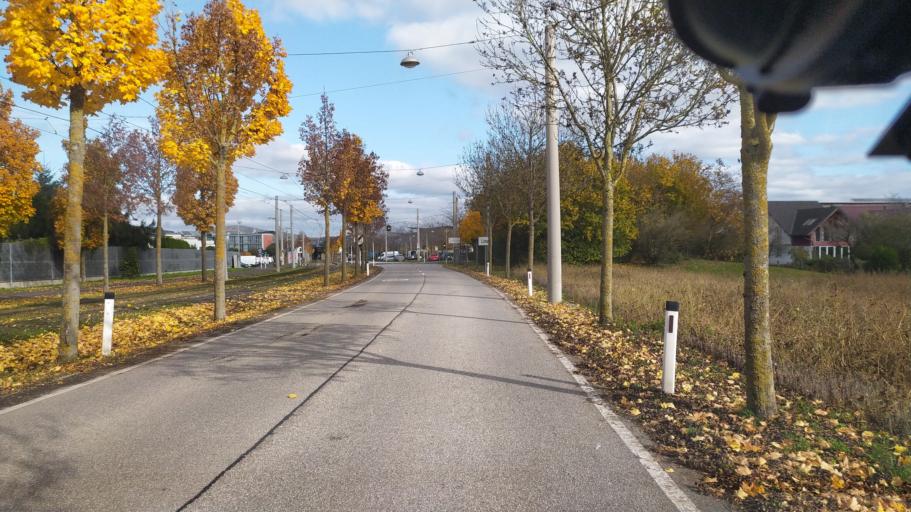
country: AT
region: Upper Austria
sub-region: Politischer Bezirk Urfahr-Umgebung
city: Steyregg
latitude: 48.2554
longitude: 14.3555
